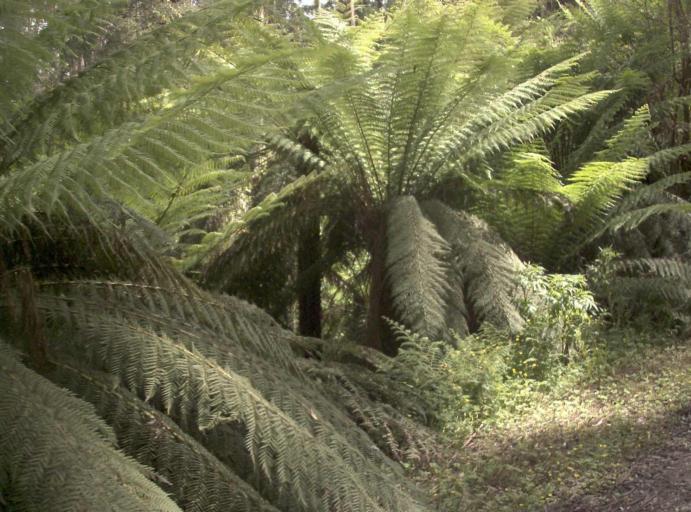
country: AU
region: Victoria
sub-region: Latrobe
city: Traralgon
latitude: -38.4219
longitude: 146.5705
